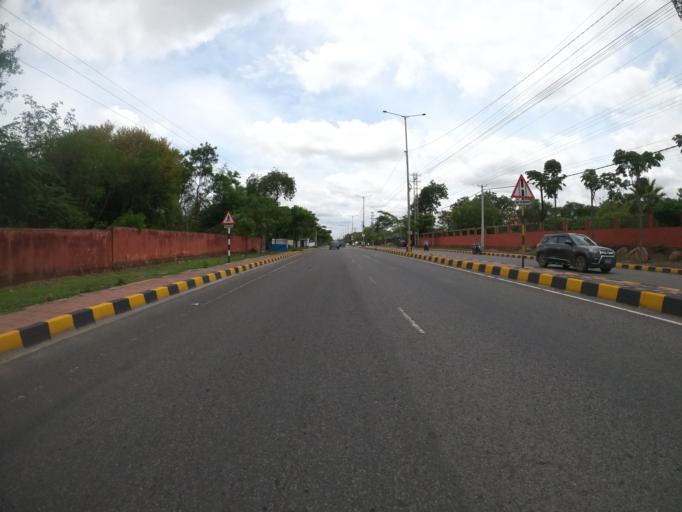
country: IN
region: Telangana
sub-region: Hyderabad
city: Hyderabad
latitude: 17.3764
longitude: 78.3889
